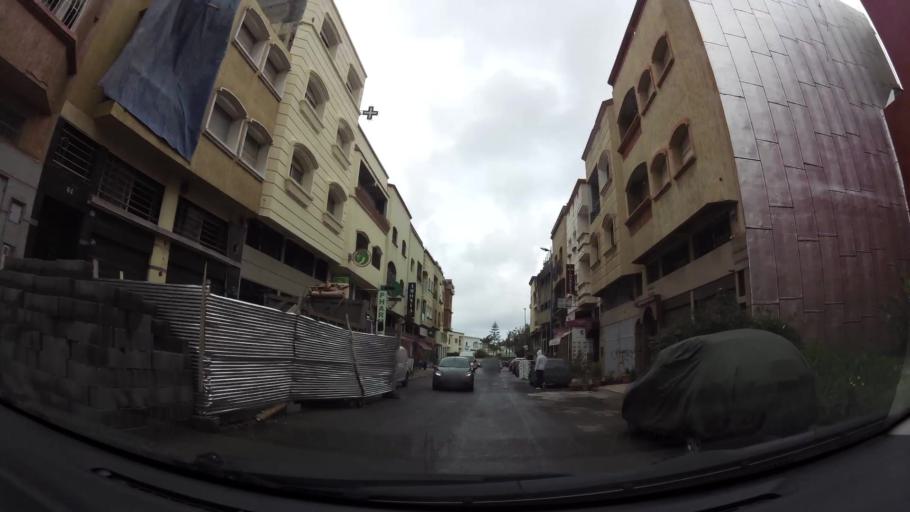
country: MA
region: Grand Casablanca
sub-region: Casablanca
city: Casablanca
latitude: 33.5389
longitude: -7.6492
